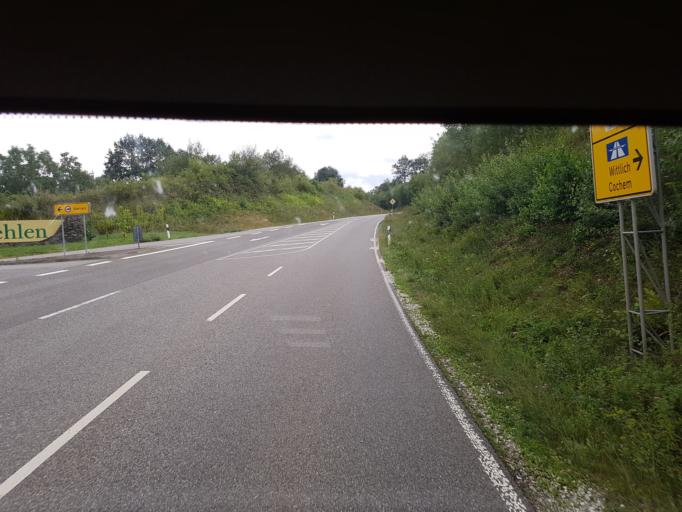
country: DE
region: Rheinland-Pfalz
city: Zeltingen-Rachtig
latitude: 49.9448
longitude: 7.0301
